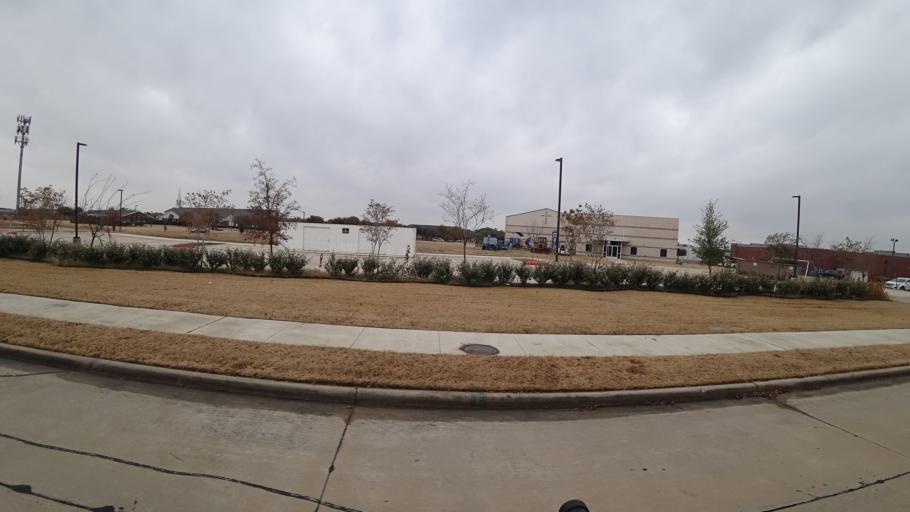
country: US
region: Texas
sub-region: Denton County
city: Lewisville
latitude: 33.0153
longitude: -96.9438
